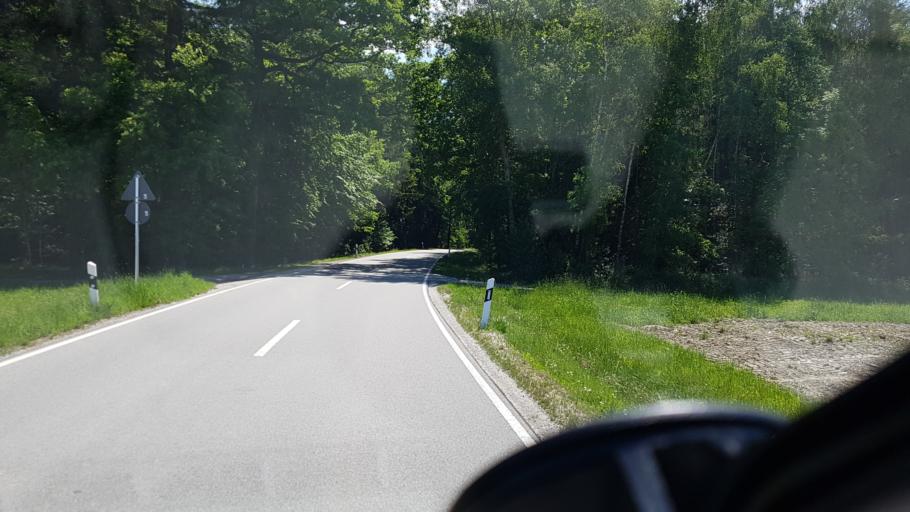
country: DE
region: Bavaria
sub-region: Lower Bavaria
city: Chostlarn
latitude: 48.3762
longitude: 13.0692
